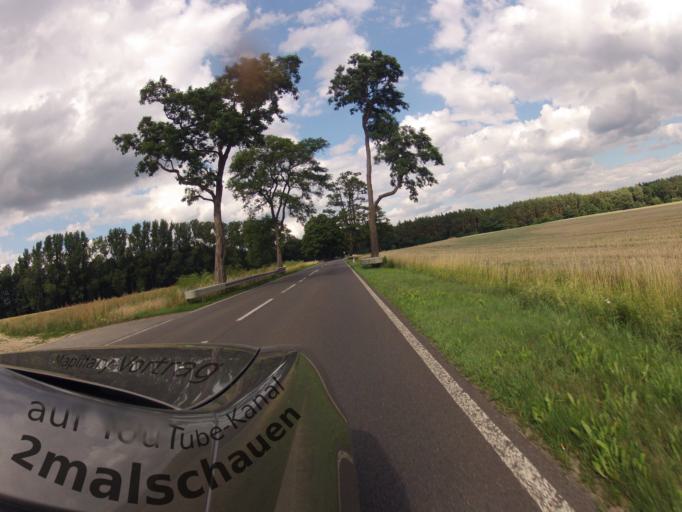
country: DE
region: Mecklenburg-Vorpommern
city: Anklam
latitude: 53.8915
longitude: 13.7232
